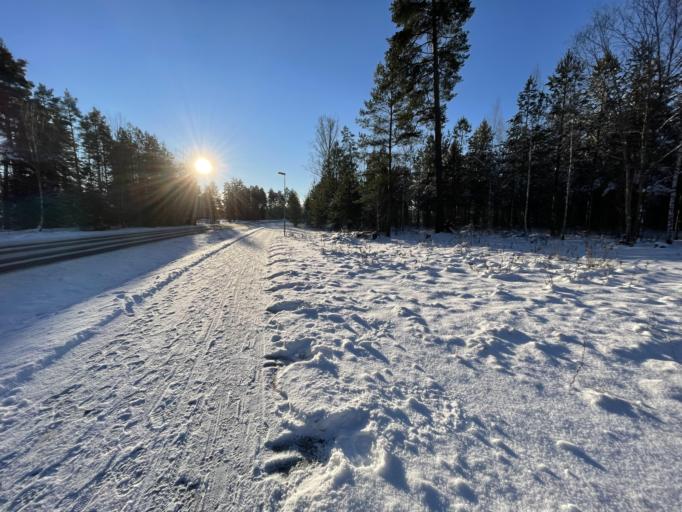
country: SE
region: Joenkoeping
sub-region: Eksjo Kommun
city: Eksjoe
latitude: 57.6416
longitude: 14.9761
